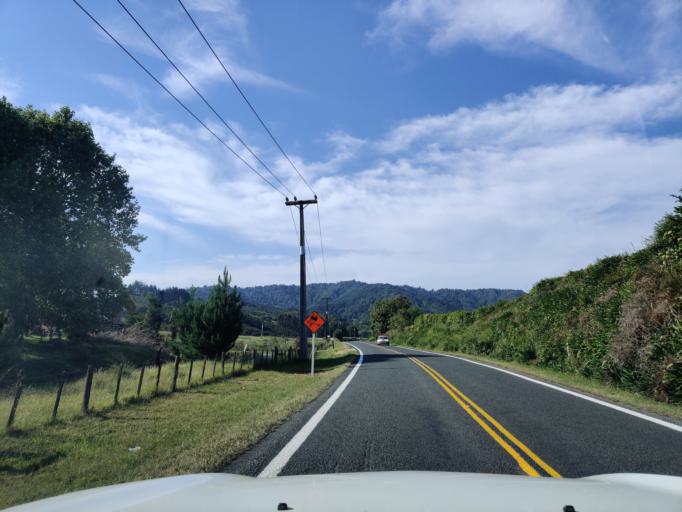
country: NZ
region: Waikato
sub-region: Waikato District
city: Ngaruawahia
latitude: -37.6482
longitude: 175.1454
